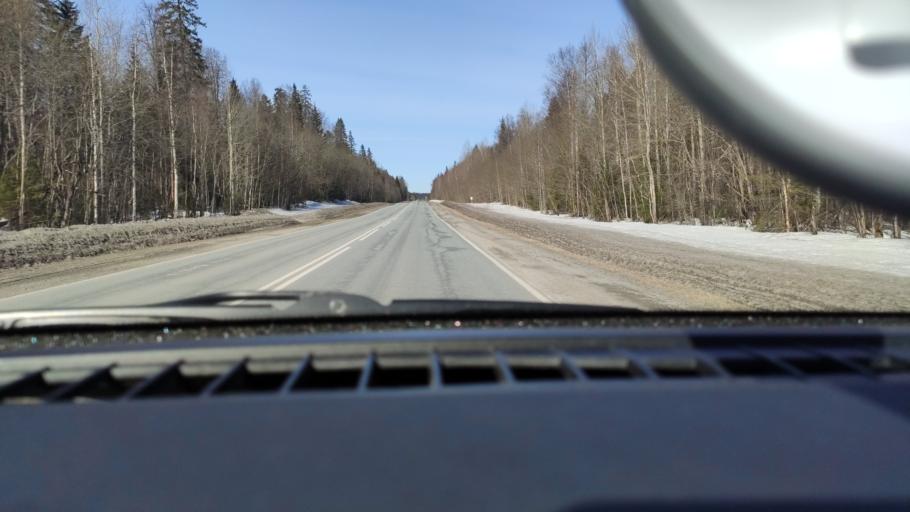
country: RU
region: Perm
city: Perm
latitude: 58.1816
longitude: 56.2241
